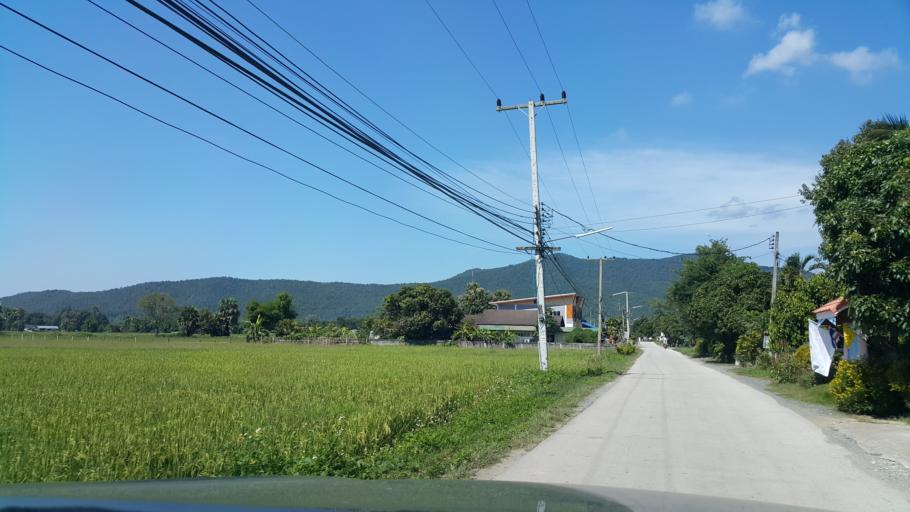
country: TH
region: Chiang Mai
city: Mae On
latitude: 18.7300
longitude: 99.2080
